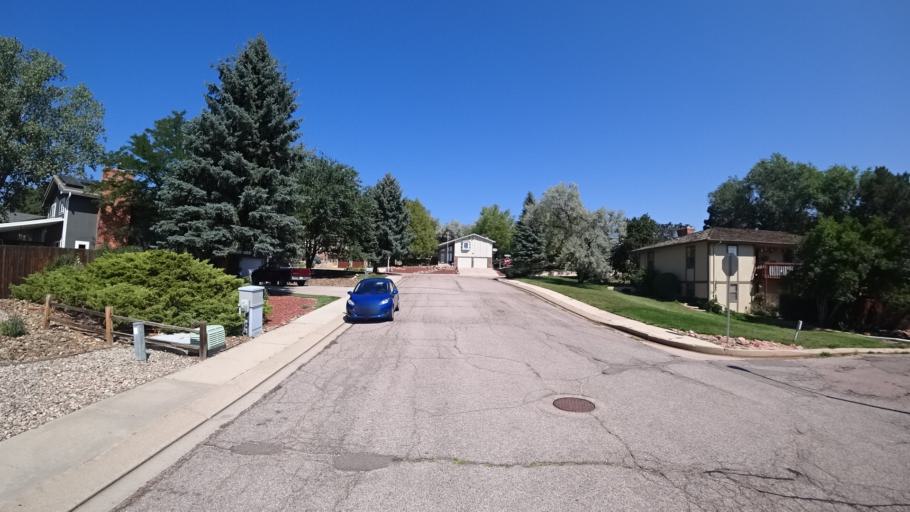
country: US
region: Colorado
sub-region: El Paso County
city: Air Force Academy
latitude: 38.9222
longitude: -104.8245
